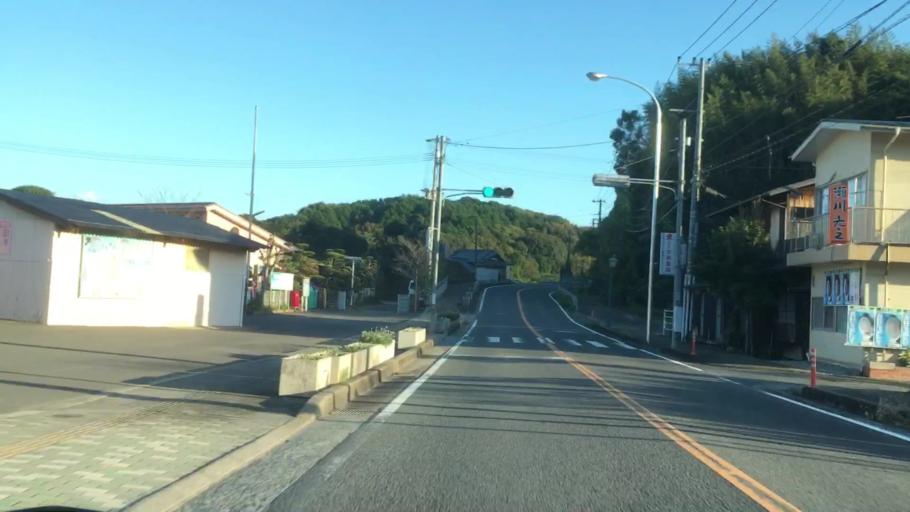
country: JP
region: Nagasaki
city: Sasebo
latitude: 33.0007
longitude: 129.7312
